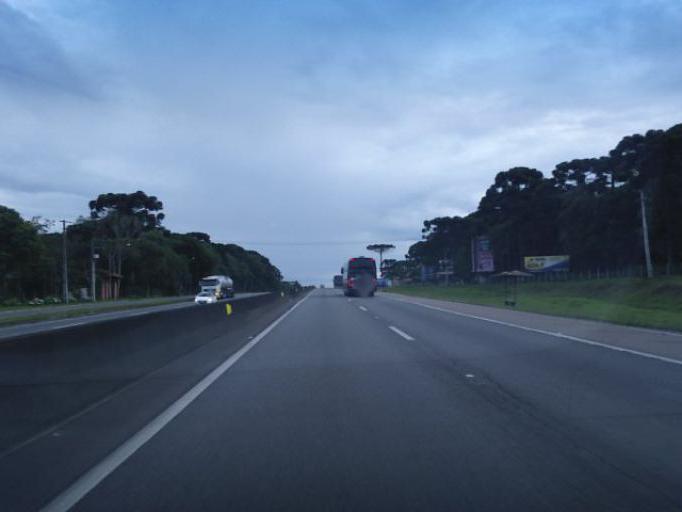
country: BR
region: Parana
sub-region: Sao Jose Dos Pinhais
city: Sao Jose dos Pinhais
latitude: -25.6454
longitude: -49.1589
